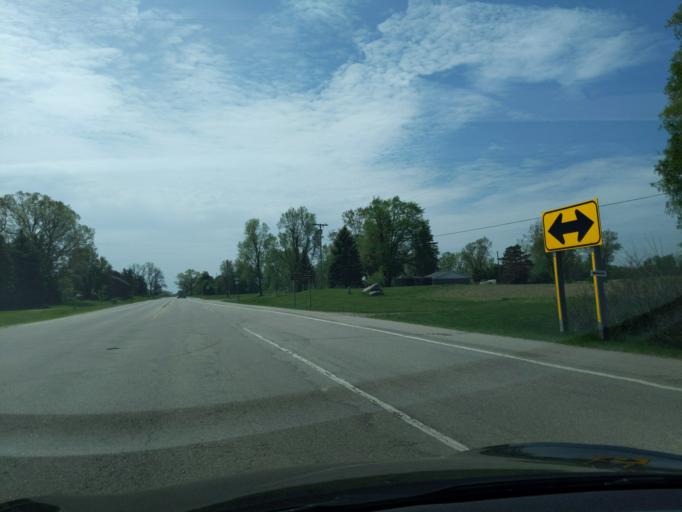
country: US
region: Michigan
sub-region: Ingham County
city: Stockbridge
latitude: 42.5115
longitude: -84.1901
